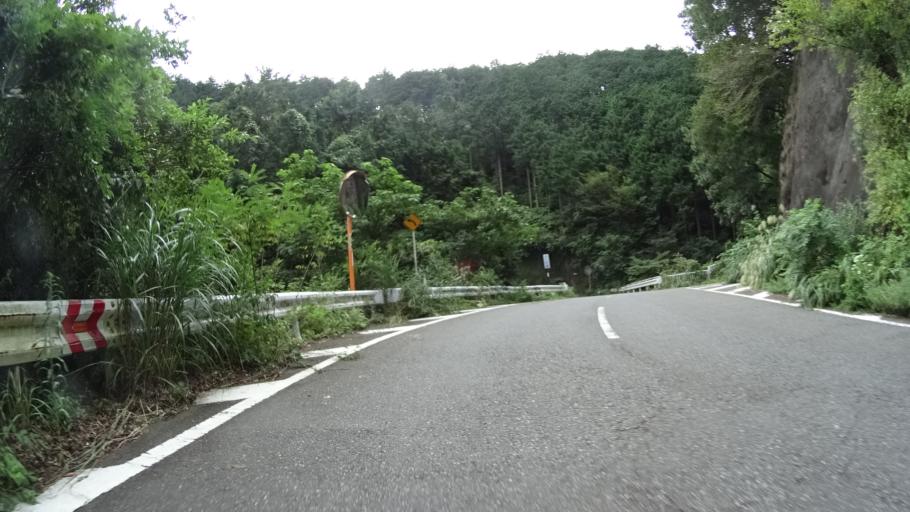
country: JP
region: Kanagawa
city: Hadano
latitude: 35.4126
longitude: 139.2173
